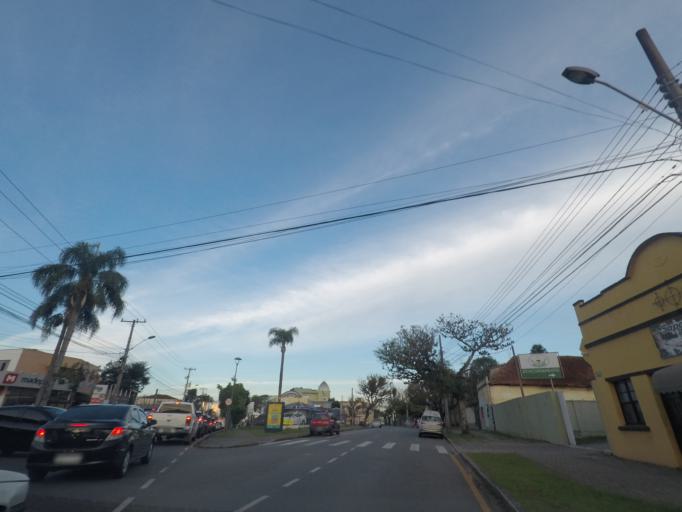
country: BR
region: Parana
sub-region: Curitiba
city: Curitiba
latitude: -25.4166
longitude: -49.2787
